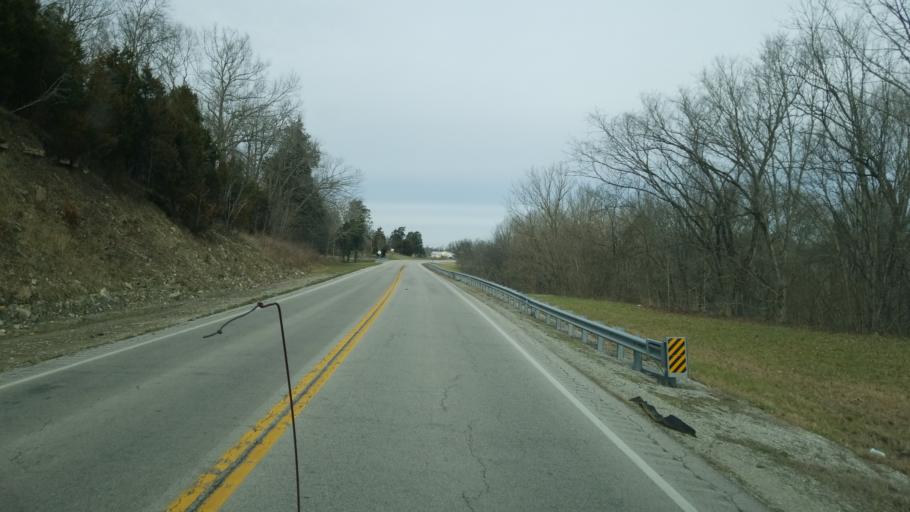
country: US
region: Kentucky
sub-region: Robertson County
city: Mount Olivet
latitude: 38.4323
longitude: -83.9911
